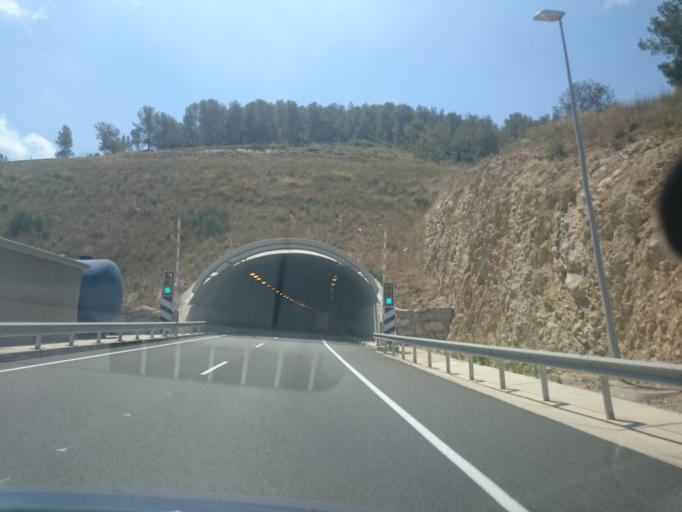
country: ES
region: Catalonia
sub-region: Provincia de Barcelona
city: Sant Pere de Ribes
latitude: 41.2752
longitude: 1.7322
